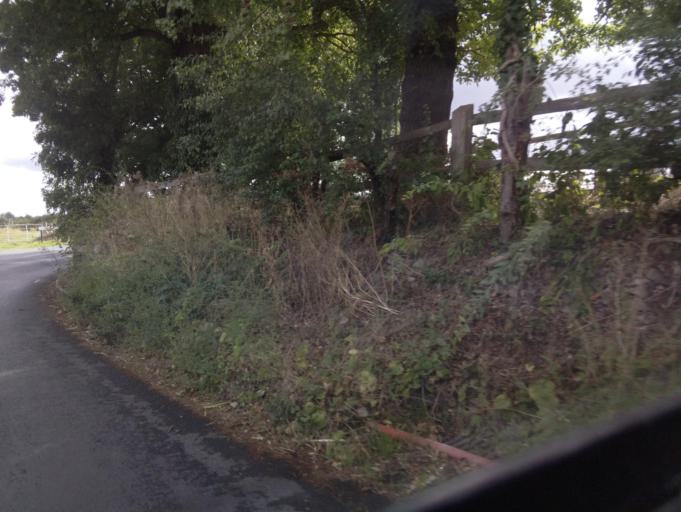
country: GB
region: England
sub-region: Leicestershire
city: Loughborough
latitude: 52.7927
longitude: -1.1948
